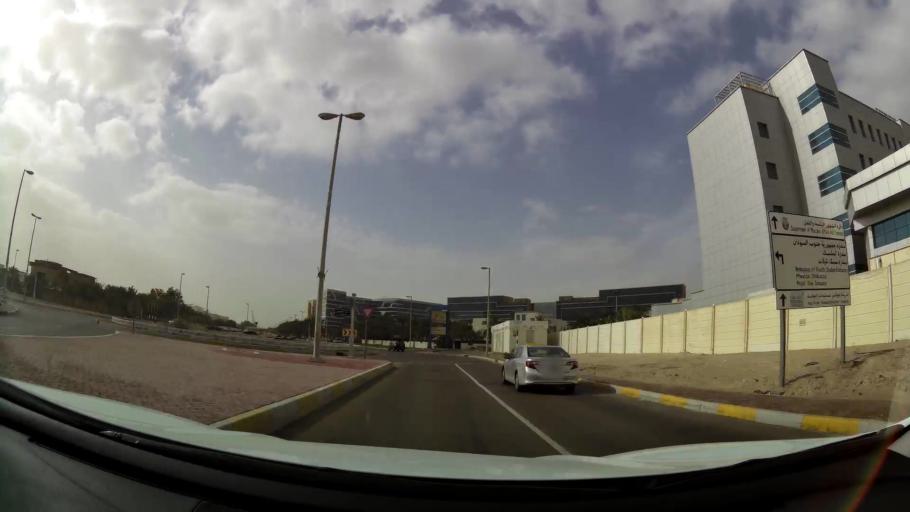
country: AE
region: Abu Dhabi
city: Abu Dhabi
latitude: 24.4171
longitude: 54.4929
